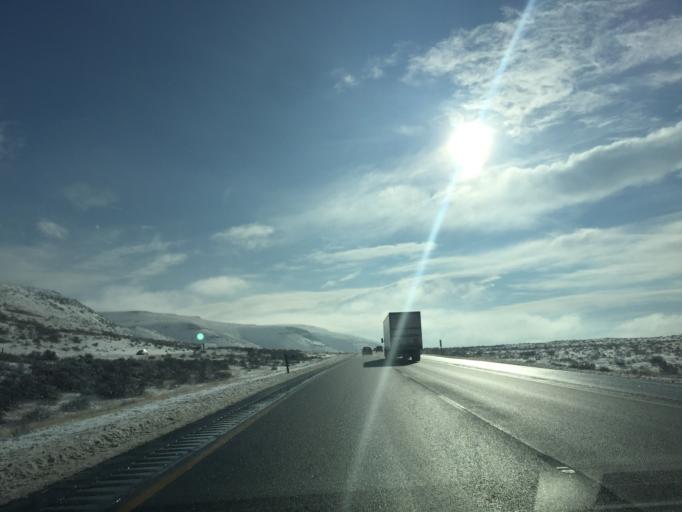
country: US
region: Washington
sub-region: Grant County
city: Mattawa
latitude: 46.9909
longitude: -119.9704
